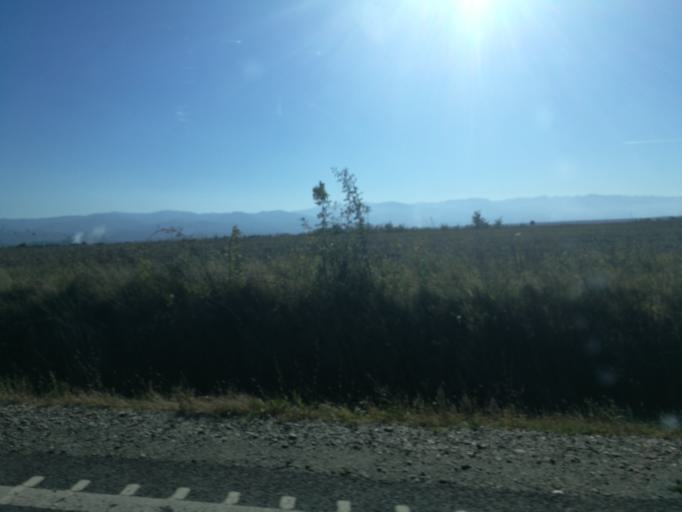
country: RO
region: Brasov
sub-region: Comuna Sercaia
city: Sercaia
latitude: 45.8108
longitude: 25.1682
